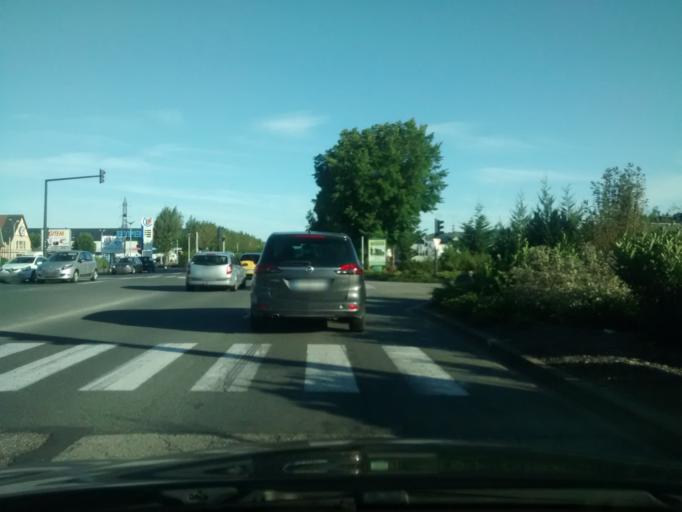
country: FR
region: Lower Normandy
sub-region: Departement du Calvados
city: Touques
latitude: 49.3437
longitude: 0.1002
